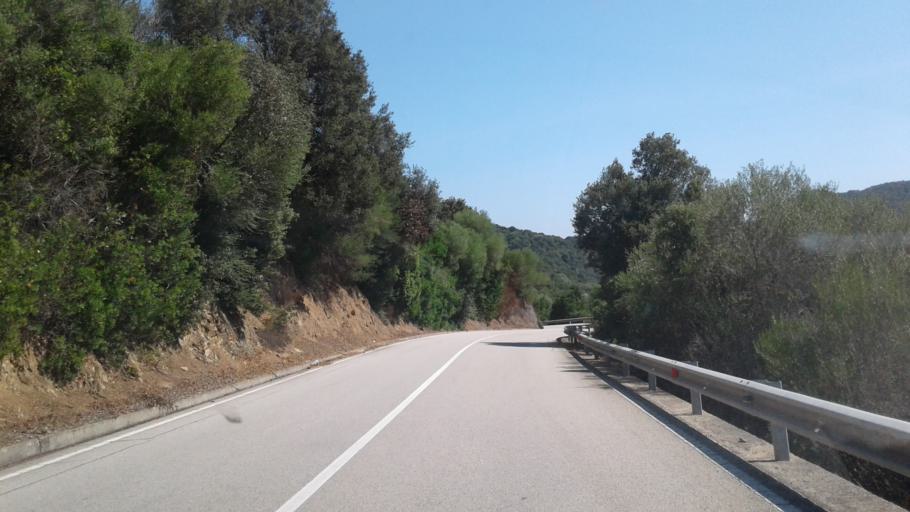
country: IT
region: Sardinia
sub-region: Provincia di Olbia-Tempio
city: Palau
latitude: 41.1344
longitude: 9.3007
